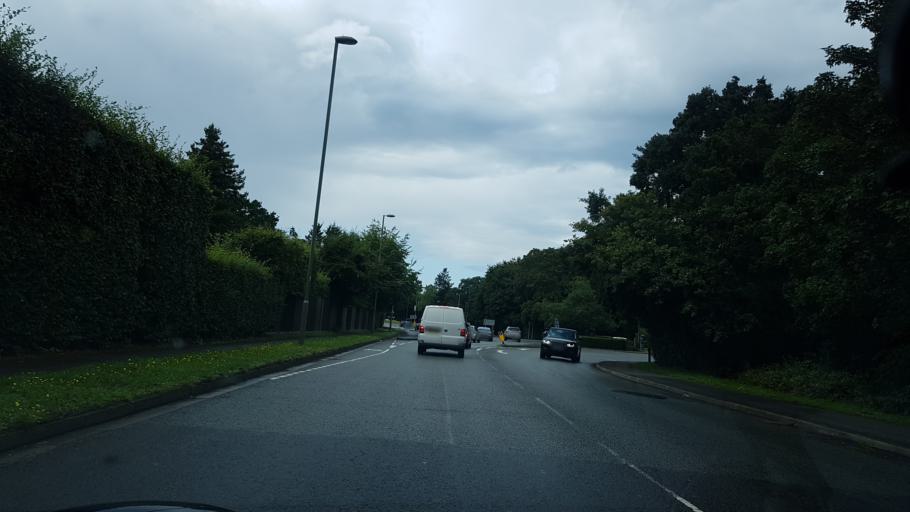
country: GB
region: England
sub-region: Surrey
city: Byfleet
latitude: 51.3403
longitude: -0.4711
